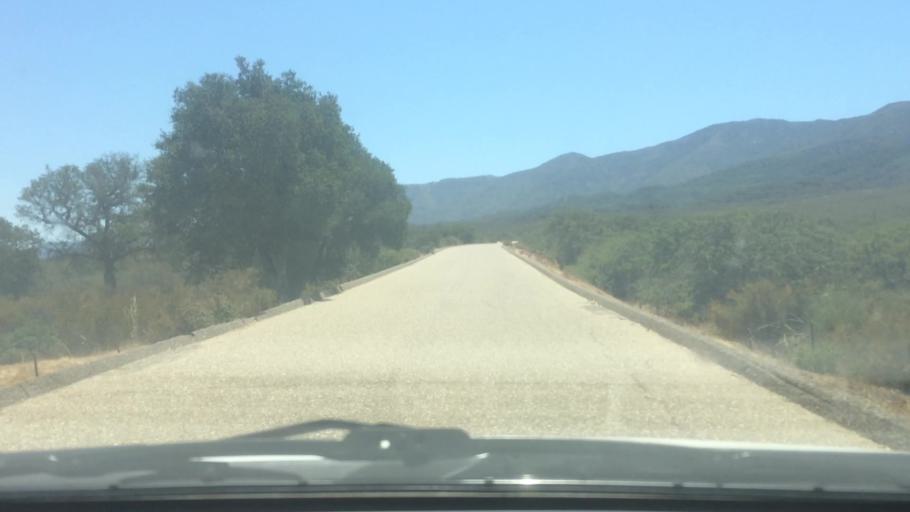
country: US
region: California
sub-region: Santa Barbara County
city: Santa Ynez
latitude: 34.5798
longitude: -119.9781
